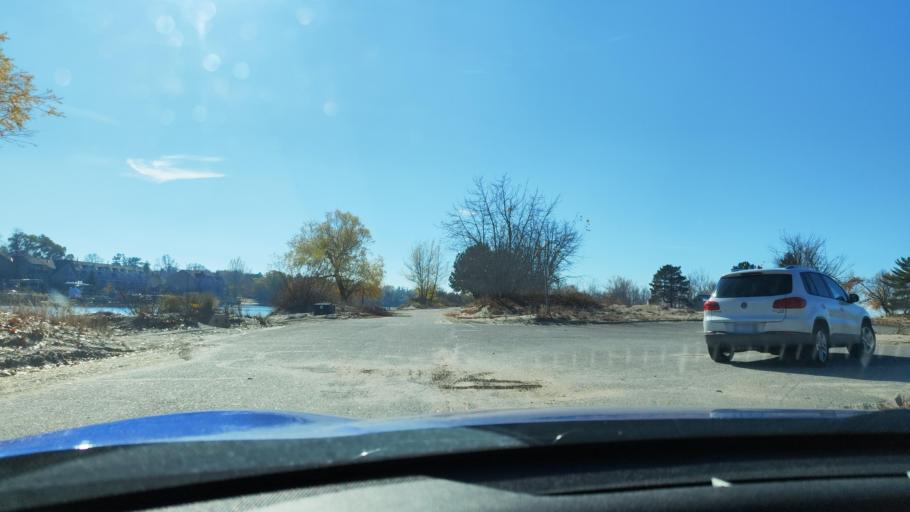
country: CA
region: Ontario
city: Wasaga Beach
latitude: 44.5320
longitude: -80.0116
